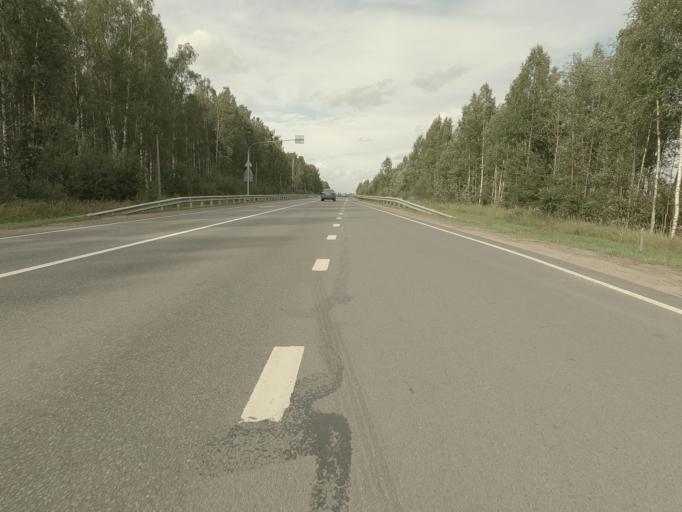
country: RU
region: Leningrad
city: Mga
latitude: 59.7867
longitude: 31.1065
